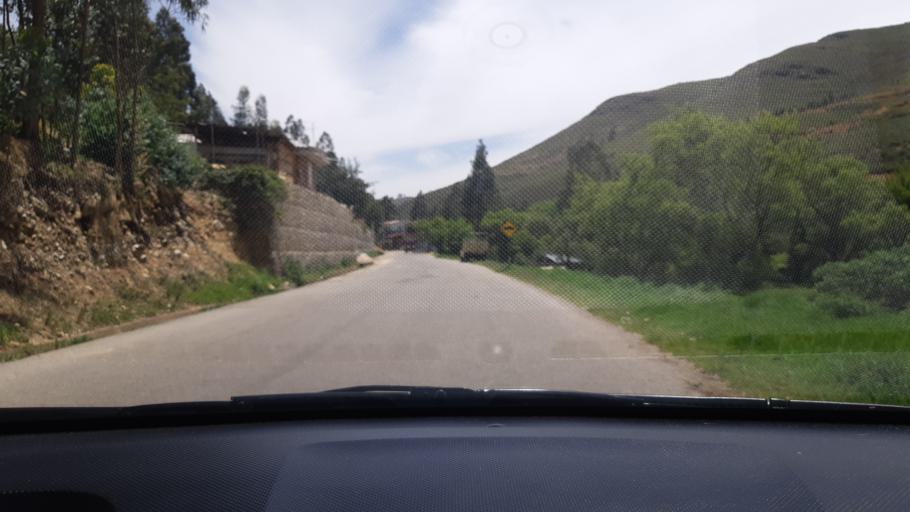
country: PE
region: Cajamarca
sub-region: Provincia de Cajamarca
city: Llacanora
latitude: -7.1851
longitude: -78.4422
